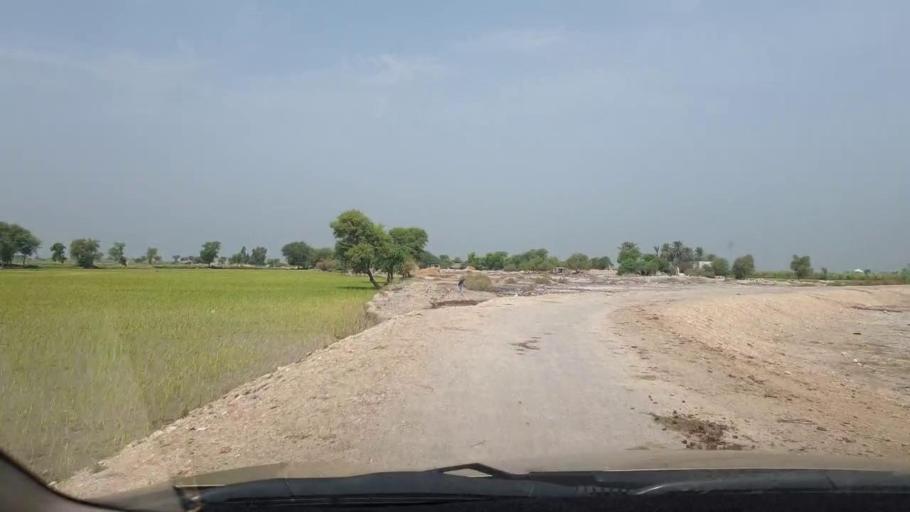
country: PK
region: Sindh
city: Goth Garelo
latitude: 27.5243
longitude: 68.0718
